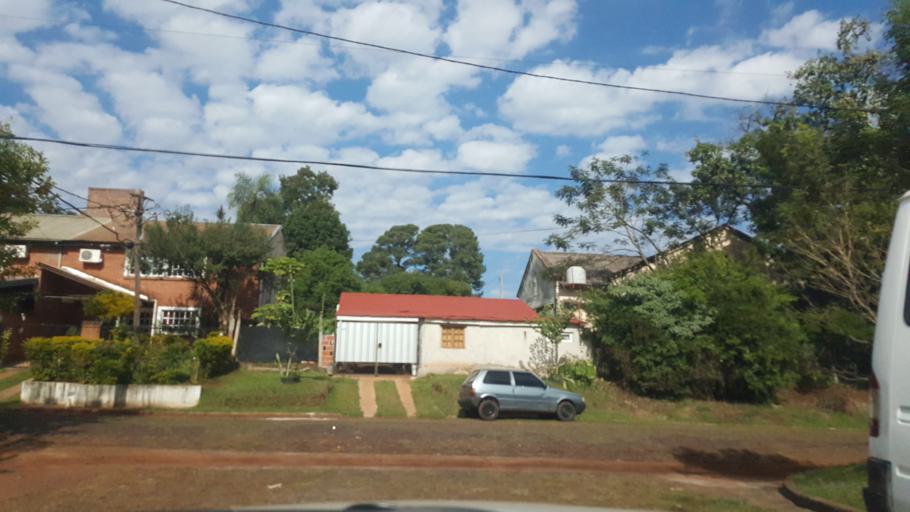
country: AR
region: Misiones
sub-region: Departamento de Capital
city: Posadas
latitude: -27.3669
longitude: -55.9230
